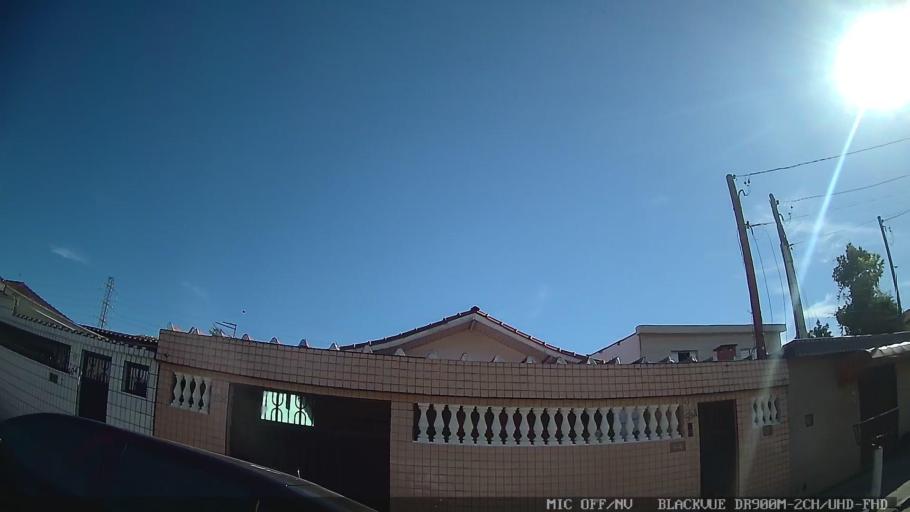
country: BR
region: Sao Paulo
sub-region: Santos
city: Santos
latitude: -23.9373
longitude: -46.2855
